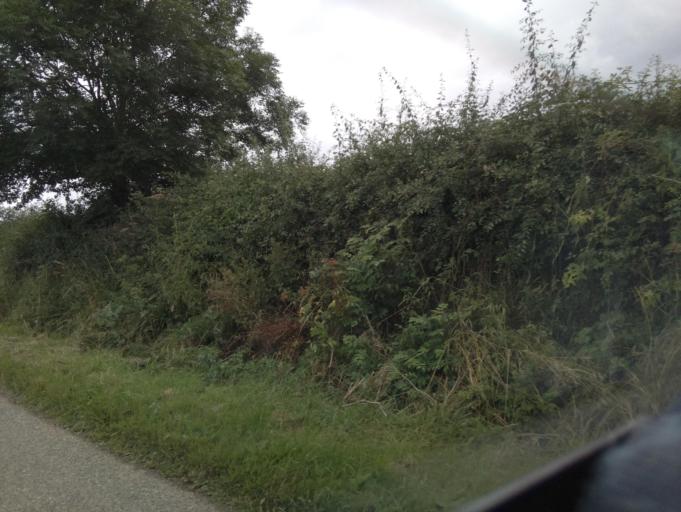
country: GB
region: England
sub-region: District of Rutland
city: Seaton
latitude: 52.5240
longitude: -0.6202
